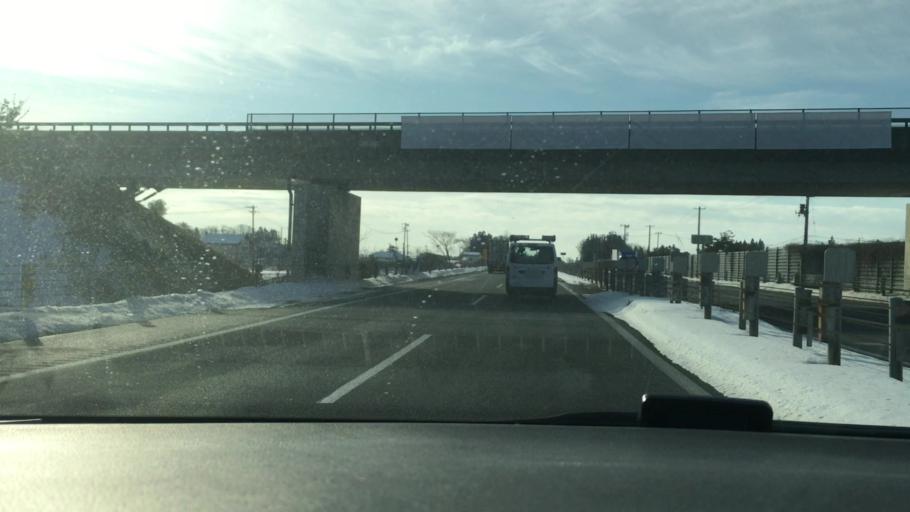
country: JP
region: Iwate
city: Hanamaki
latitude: 39.4016
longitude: 141.0925
